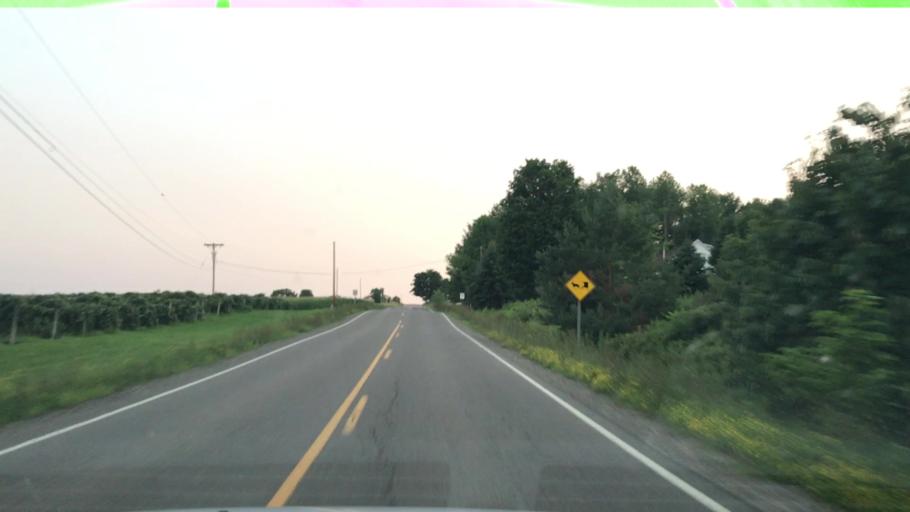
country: US
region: New York
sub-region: Steuben County
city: Sylvan Beach
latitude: 42.5197
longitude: -77.1708
